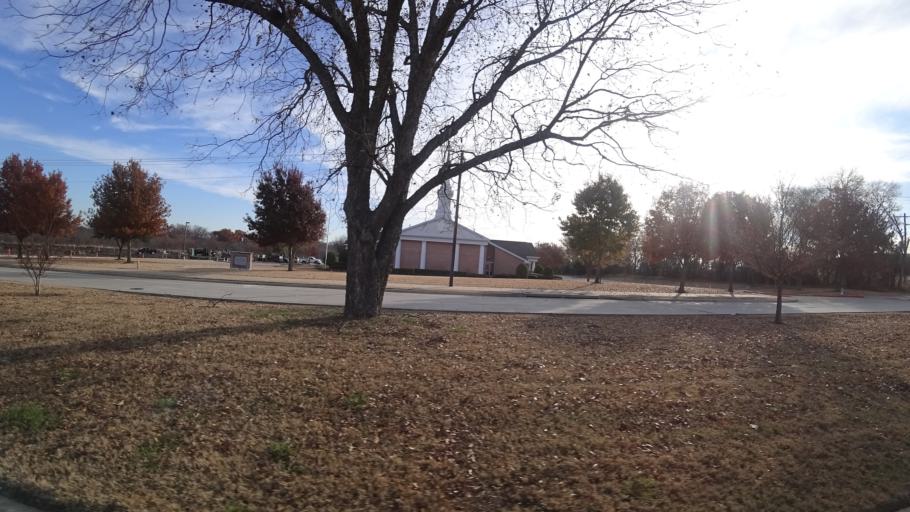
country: US
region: Texas
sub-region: Collin County
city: McKinney
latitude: 33.2068
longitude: -96.6798
